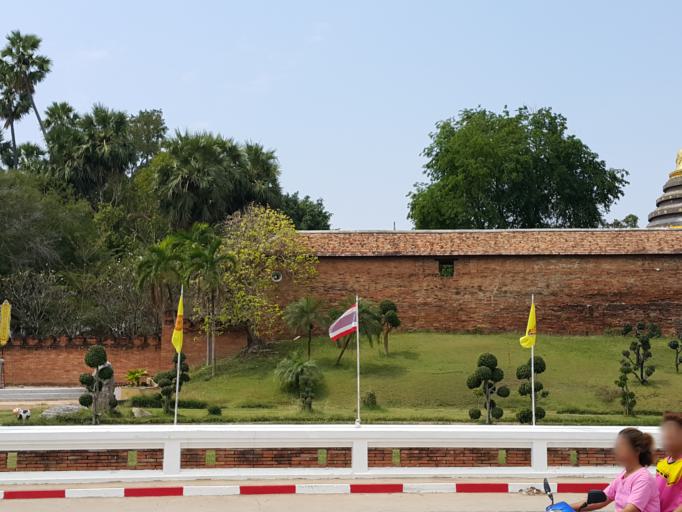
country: TH
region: Lampang
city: Ko Kha
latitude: 18.2169
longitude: 99.3899
